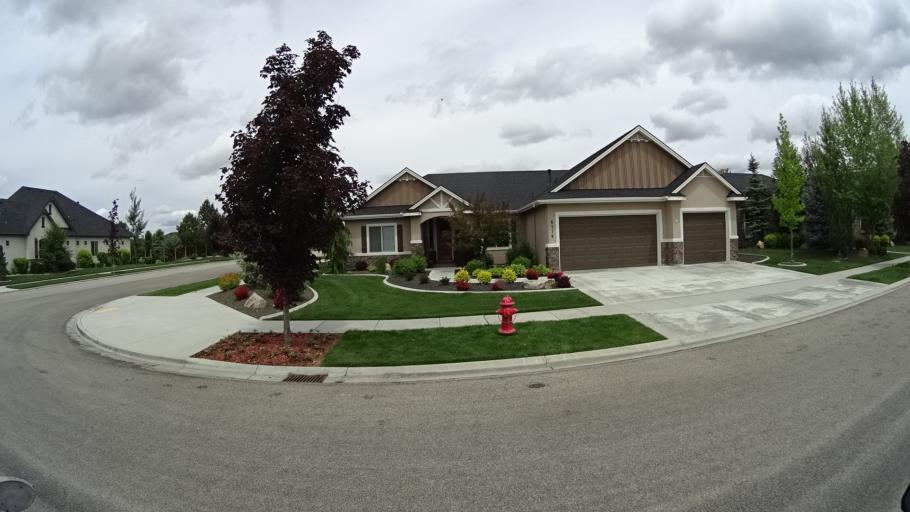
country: US
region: Idaho
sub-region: Ada County
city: Star
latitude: 43.7056
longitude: -116.4302
